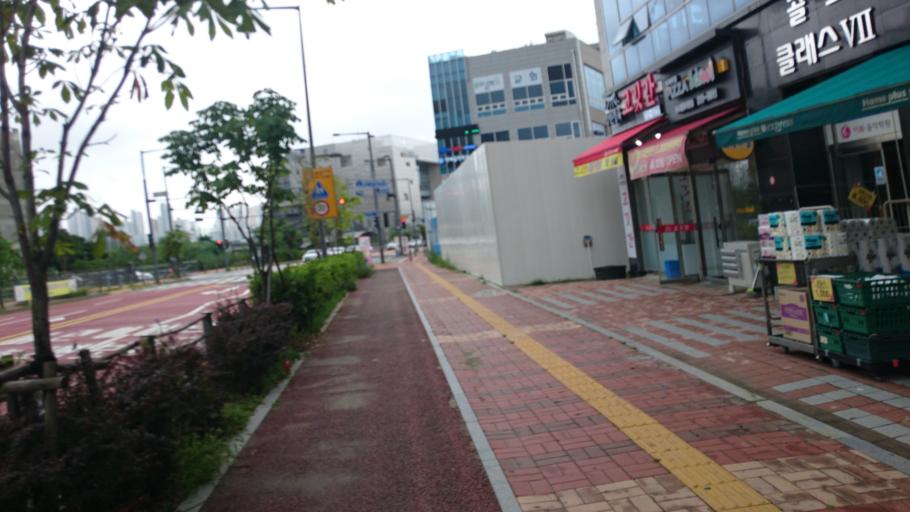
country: KR
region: Gyeonggi-do
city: Suwon-si
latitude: 37.3048
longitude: 127.0473
